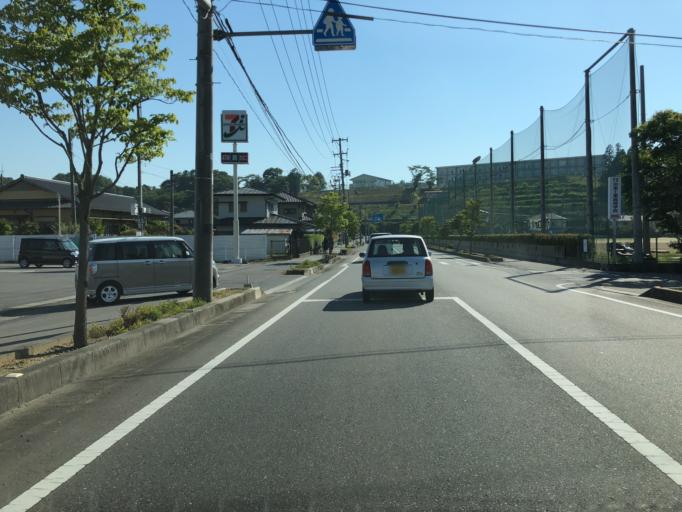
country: JP
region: Ibaraki
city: Kitaibaraki
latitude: 36.9273
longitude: 140.7943
